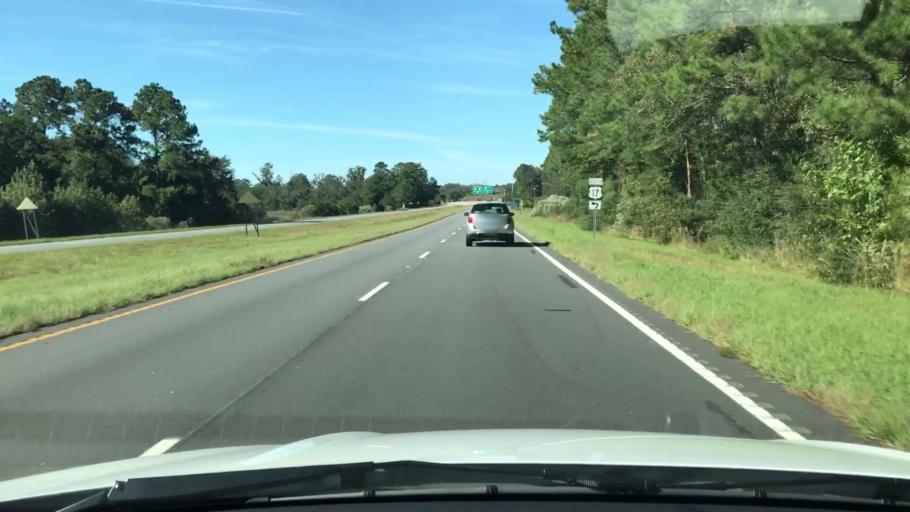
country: US
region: South Carolina
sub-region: Hampton County
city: Yemassee
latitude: 32.5959
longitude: -80.7540
